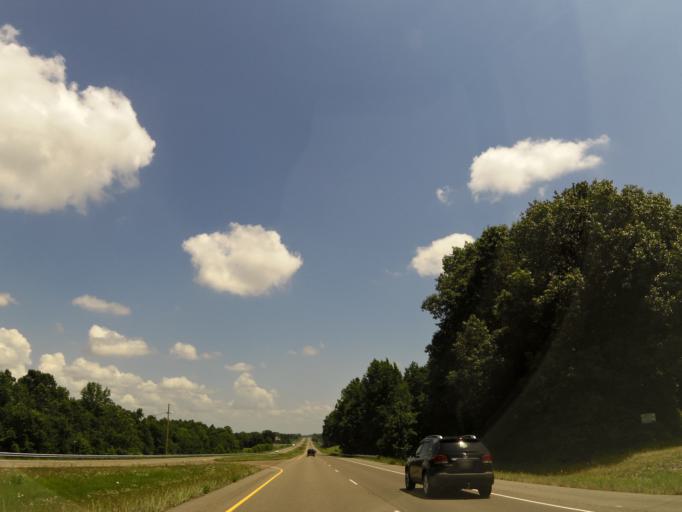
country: US
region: Tennessee
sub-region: Lauderdale County
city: Halls
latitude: 35.9073
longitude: -89.2587
